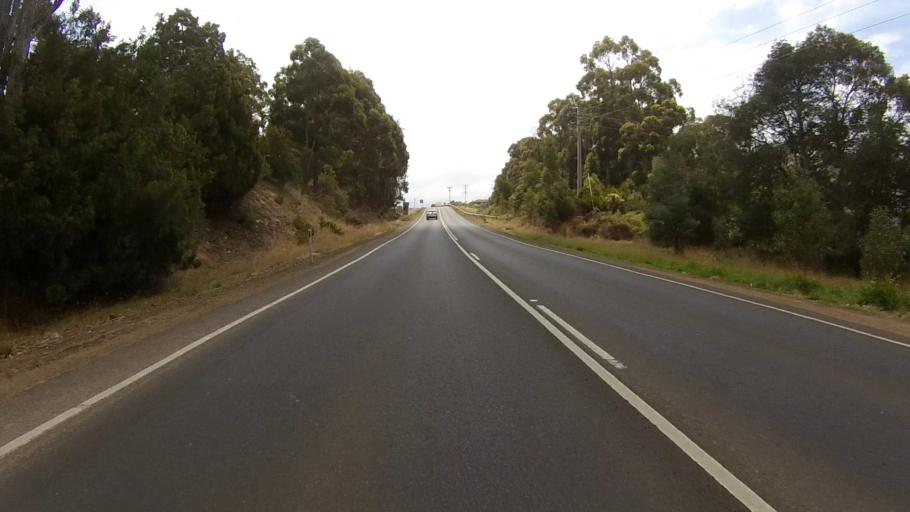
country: AU
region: Tasmania
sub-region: Kingborough
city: Margate
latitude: -43.0723
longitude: 147.2565
